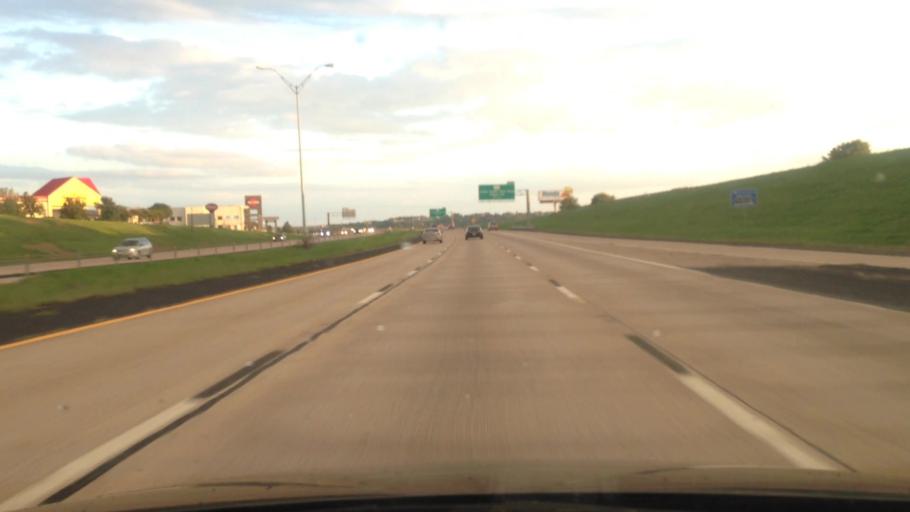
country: US
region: Texas
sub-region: Tarrant County
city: White Settlement
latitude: 32.7328
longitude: -97.4815
